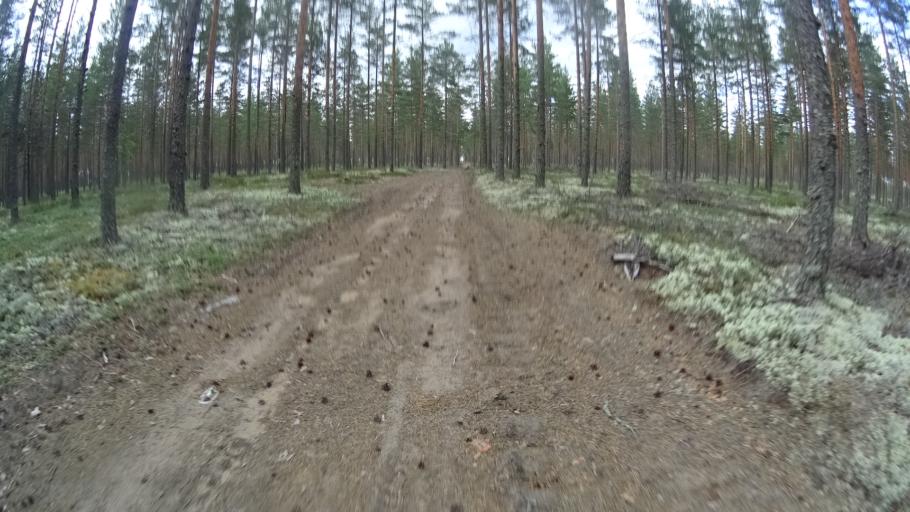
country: FI
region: Satakunta
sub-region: Pohjois-Satakunta
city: Jaemijaervi
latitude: 61.7674
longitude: 22.8020
